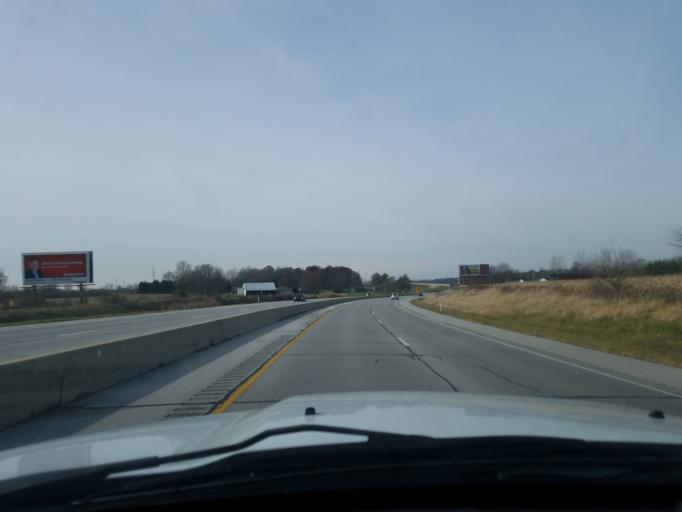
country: US
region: Indiana
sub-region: Delaware County
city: Yorktown
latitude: 40.2192
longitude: -85.5145
